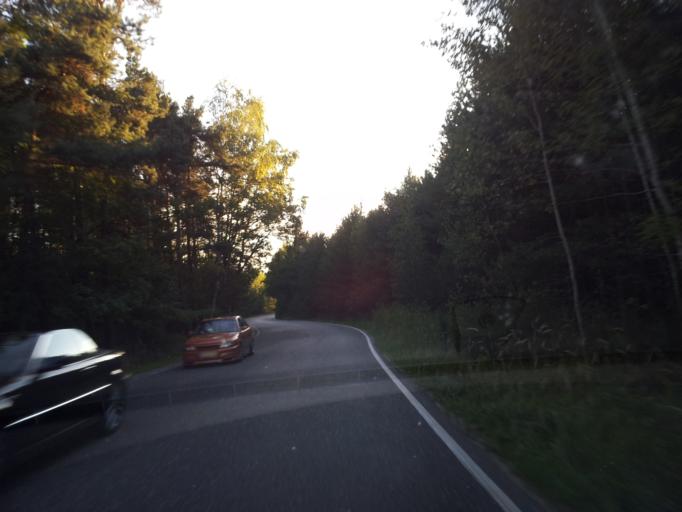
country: DE
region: Saxony
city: Ottendorf-Okrilla
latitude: 51.1942
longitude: 13.8178
